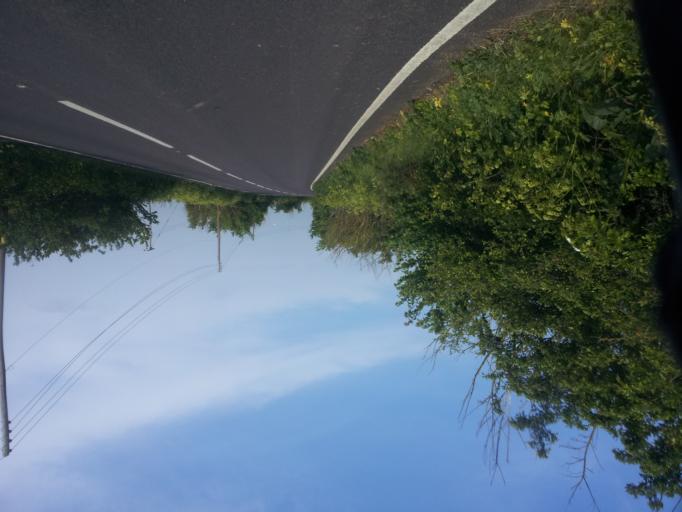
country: GB
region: England
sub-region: Kent
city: Queenborough
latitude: 51.4095
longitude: 0.7675
